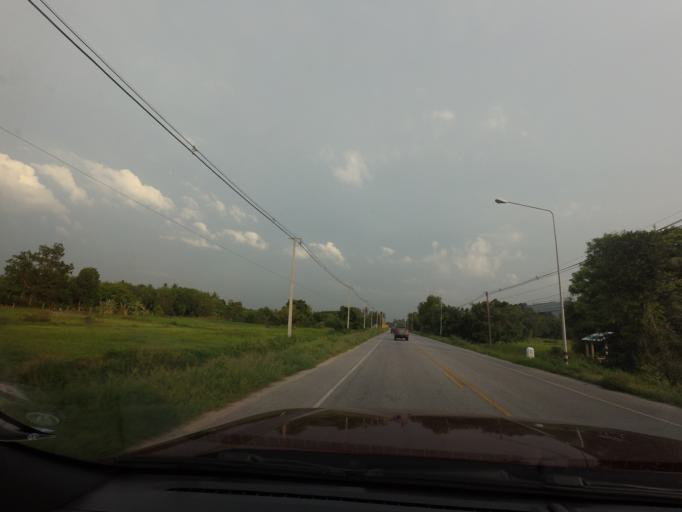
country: TH
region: Pattani
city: Mae Lan
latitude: 6.6257
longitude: 101.1879
